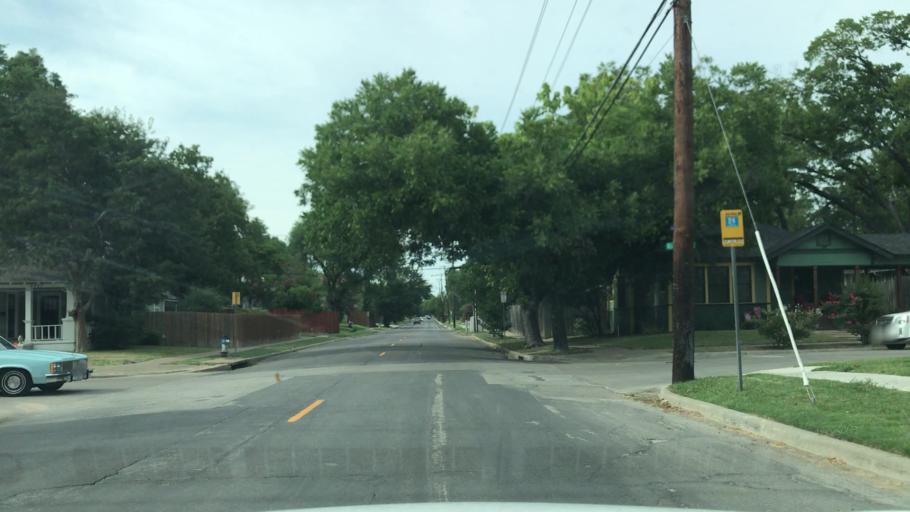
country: US
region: Texas
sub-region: Dallas County
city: Highland Park
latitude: 32.8190
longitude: -96.7748
